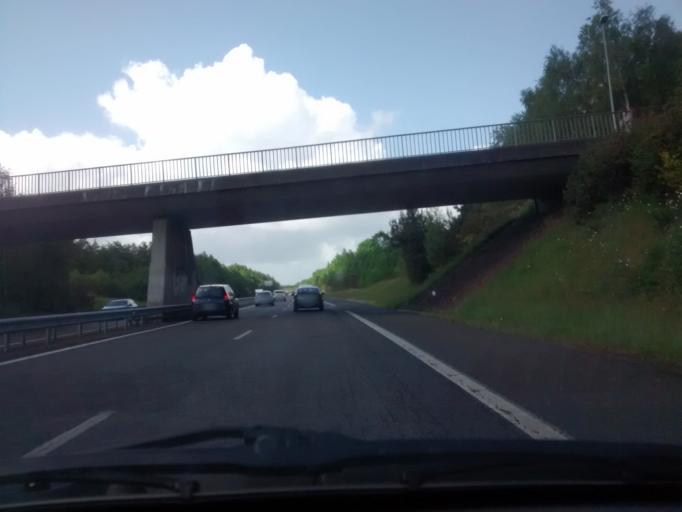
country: FR
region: Brittany
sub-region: Departement d'Ille-et-Vilaine
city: Plelan-le-Grand
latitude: 48.0044
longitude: -2.0857
